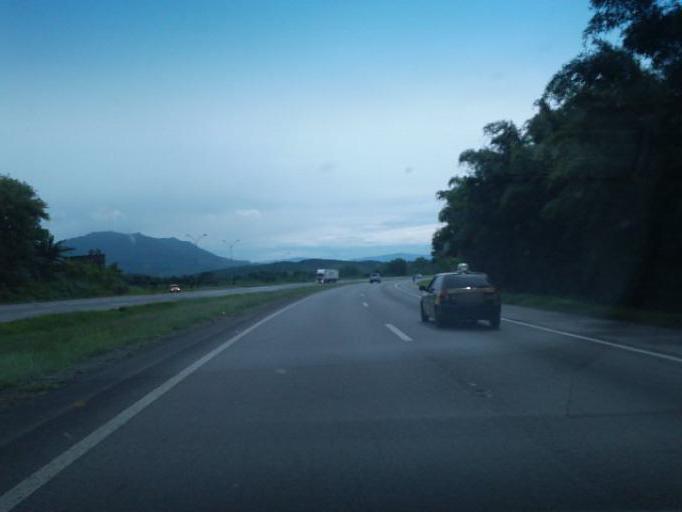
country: BR
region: Sao Paulo
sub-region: Jacupiranga
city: Jacupiranga
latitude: -24.7223
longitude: -48.0442
